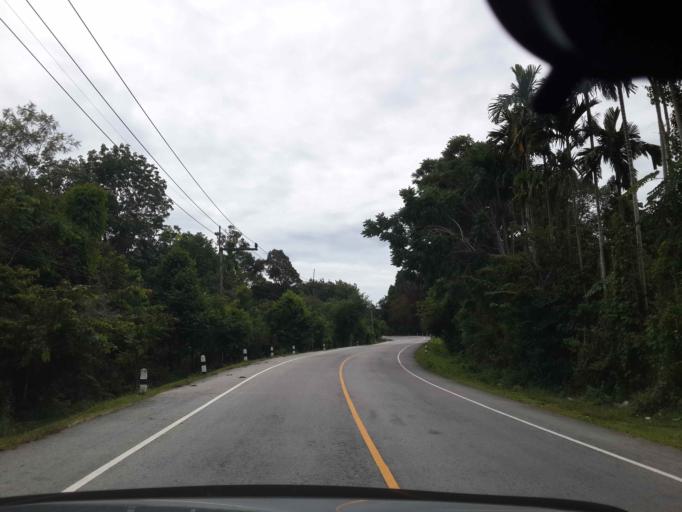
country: TH
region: Narathiwat
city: Rueso
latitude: 6.3546
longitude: 101.5678
